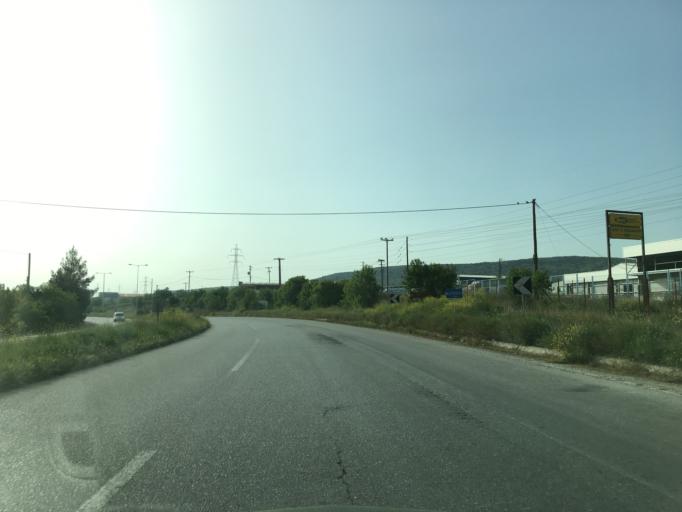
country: GR
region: Thessaly
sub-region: Nomos Magnisias
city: Nea Ionia
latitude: 39.3842
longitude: 22.8496
